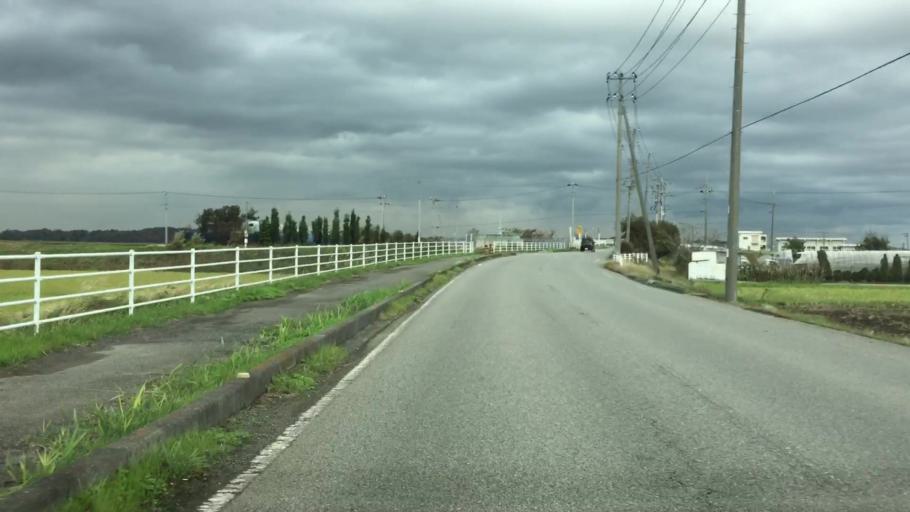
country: JP
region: Chiba
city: Shiroi
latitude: 35.8457
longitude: 140.0971
